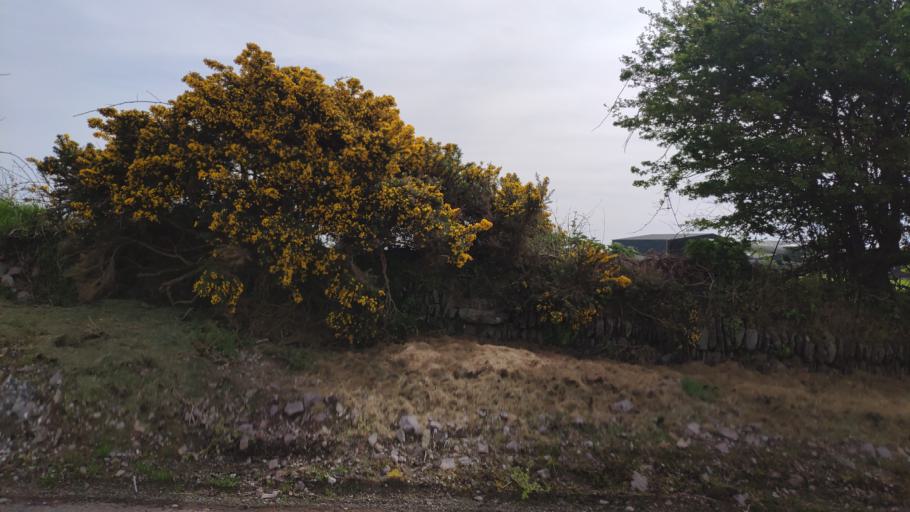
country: IE
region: Munster
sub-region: County Cork
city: Blarney
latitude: 51.9770
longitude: -8.5133
